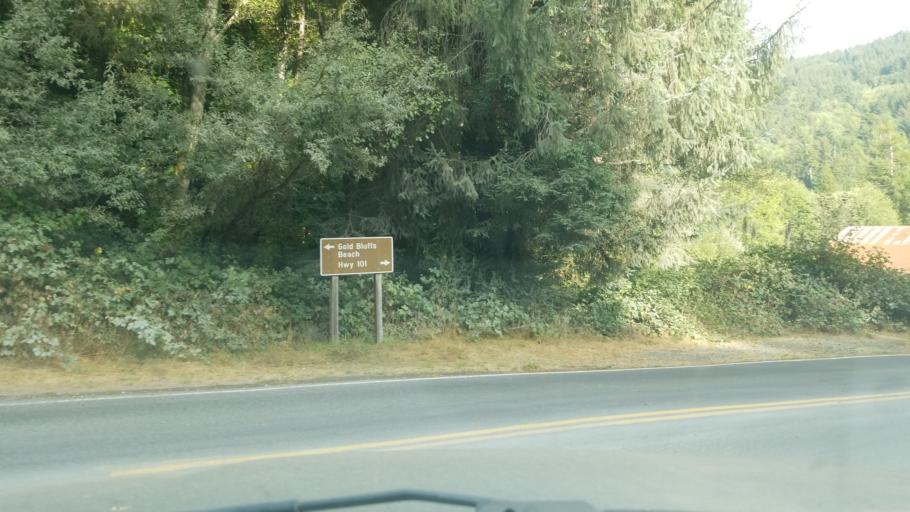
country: US
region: California
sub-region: Humboldt County
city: Westhaven-Moonstone
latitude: 41.3239
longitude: -124.0438
